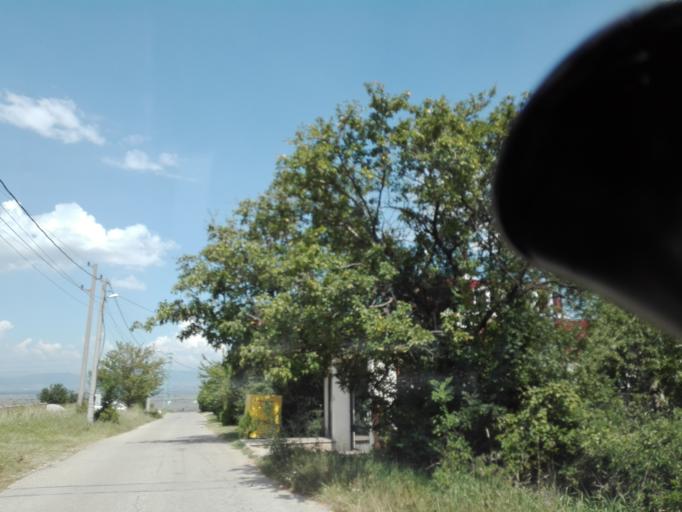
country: BG
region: Sofiya
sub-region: Obshtina Elin Pelin
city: Elin Pelin
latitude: 42.6039
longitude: 23.4847
